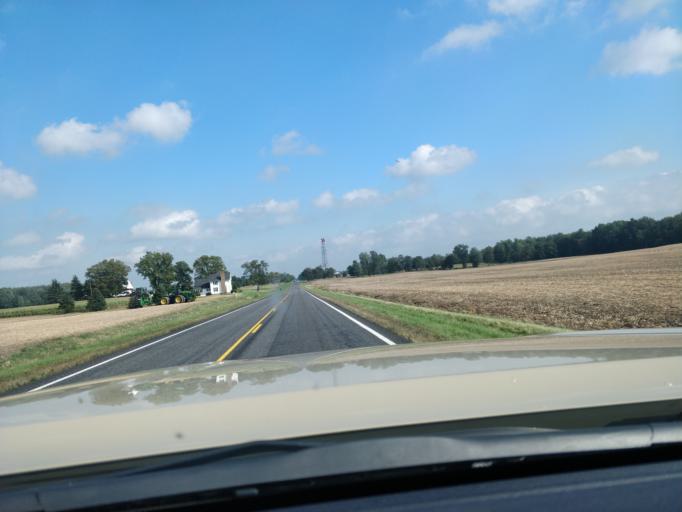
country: US
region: Michigan
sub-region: Ionia County
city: Saranac
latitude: 42.8861
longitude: -85.1705
